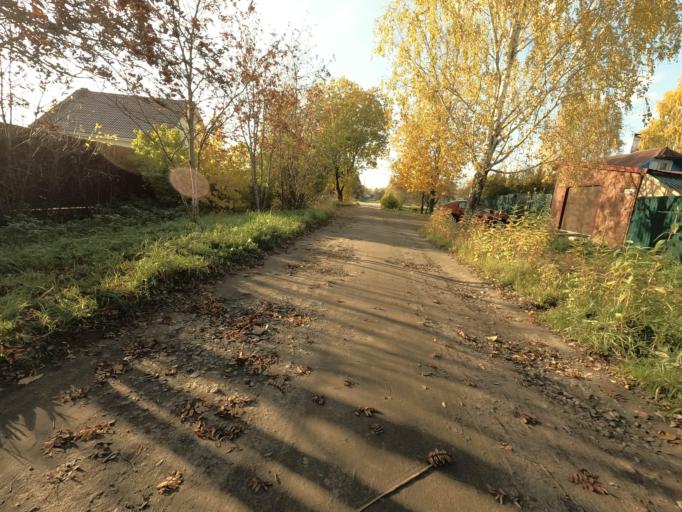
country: RU
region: Leningrad
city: Mga
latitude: 59.7531
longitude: 31.0544
